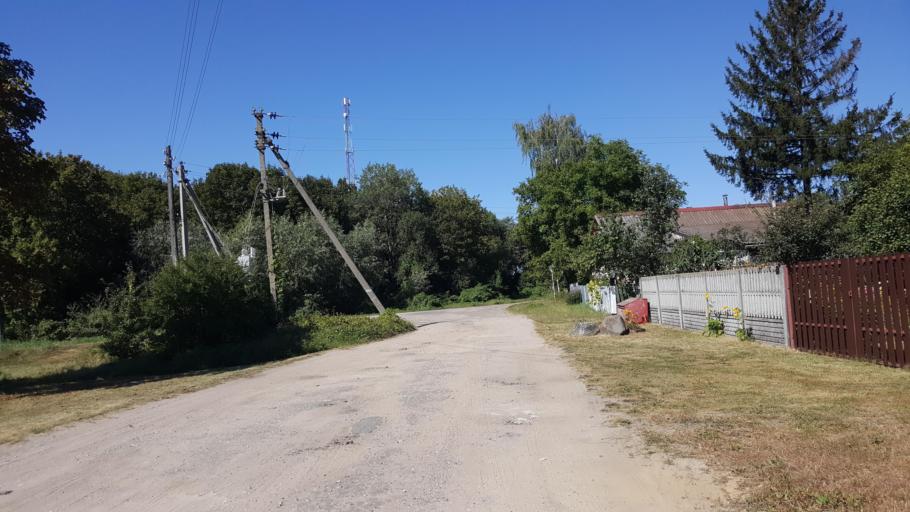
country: BY
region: Brest
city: Vysokaye
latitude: 52.2352
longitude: 23.4953
